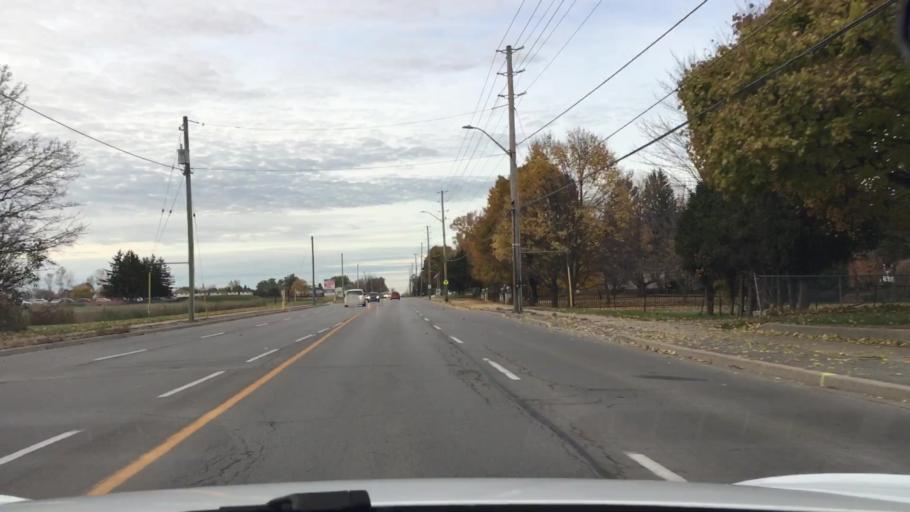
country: CA
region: Ontario
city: Oshawa
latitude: 43.9102
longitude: -78.8150
